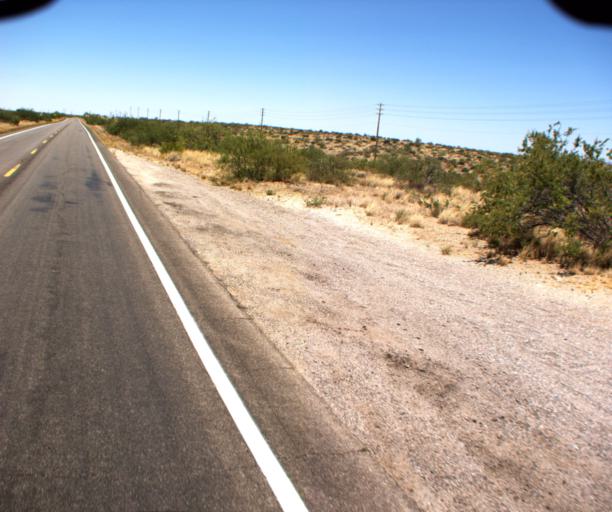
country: US
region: Arizona
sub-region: Pima County
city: Catalina
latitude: 32.5847
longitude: -110.9588
